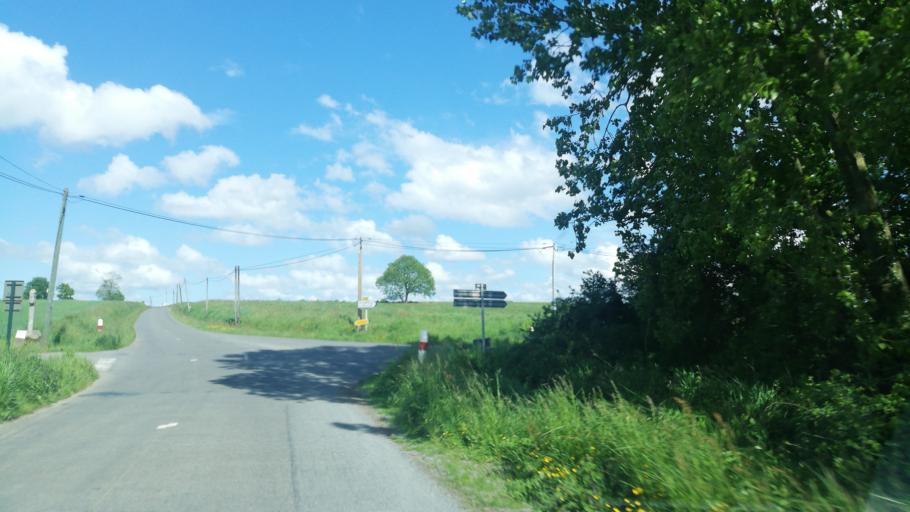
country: FR
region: Brittany
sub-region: Departement d'Ille-et-Vilaine
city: Montauban-de-Bretagne
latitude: 48.2227
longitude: -2.0001
